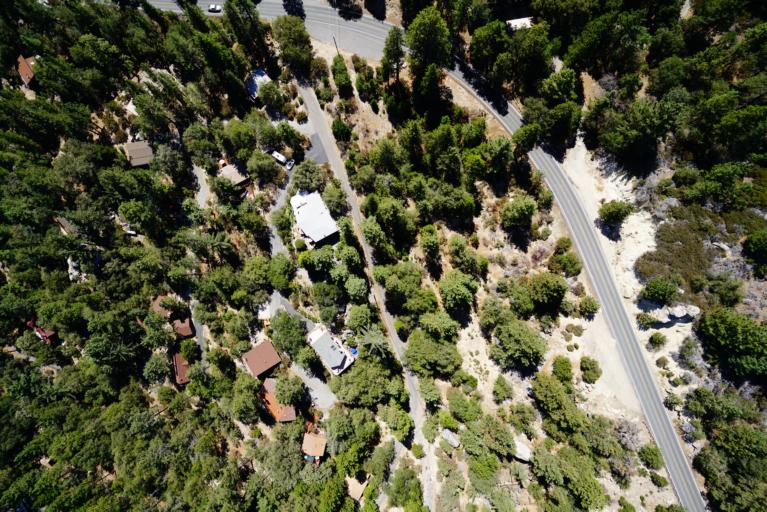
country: US
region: California
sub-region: Riverside County
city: Idyllwild-Pine Cove
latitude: 33.7528
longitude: -116.7352
